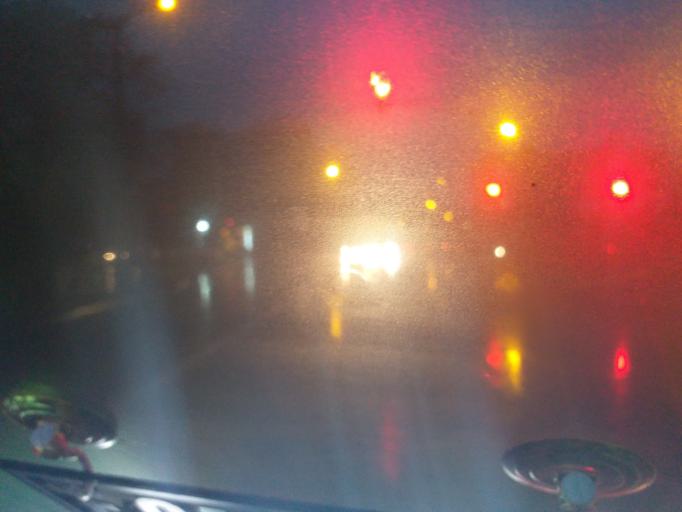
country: TR
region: Ankara
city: Ankara
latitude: 39.9420
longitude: 32.8249
